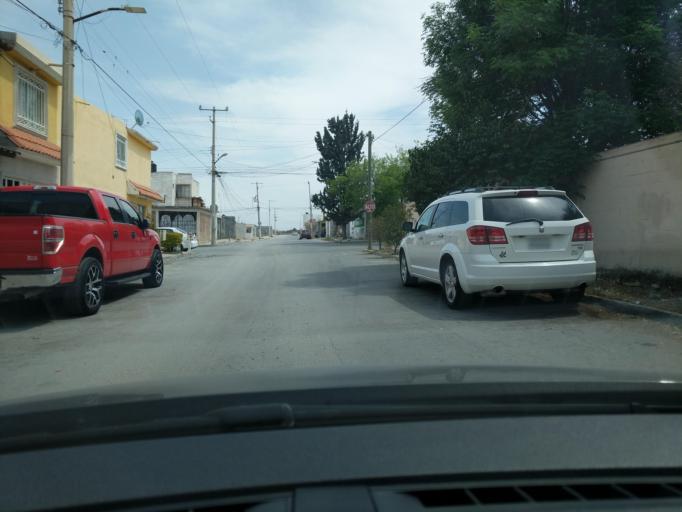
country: MX
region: Coahuila
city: Saltillo
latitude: 25.4062
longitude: -100.9379
